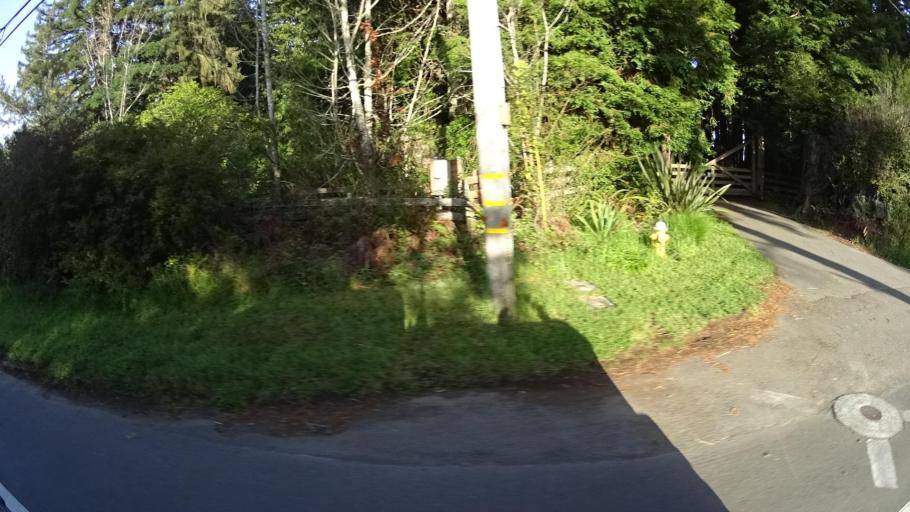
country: US
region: California
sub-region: Humboldt County
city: Myrtletown
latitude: 40.7742
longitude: -124.0737
